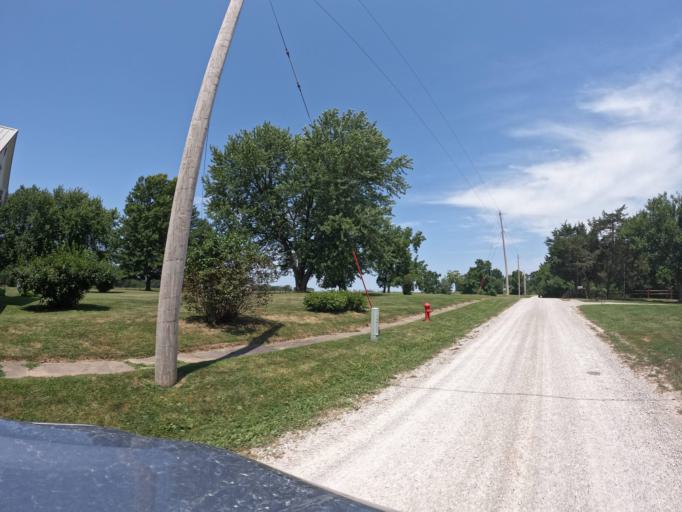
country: US
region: Iowa
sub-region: Appanoose County
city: Centerville
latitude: 40.7809
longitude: -92.9495
